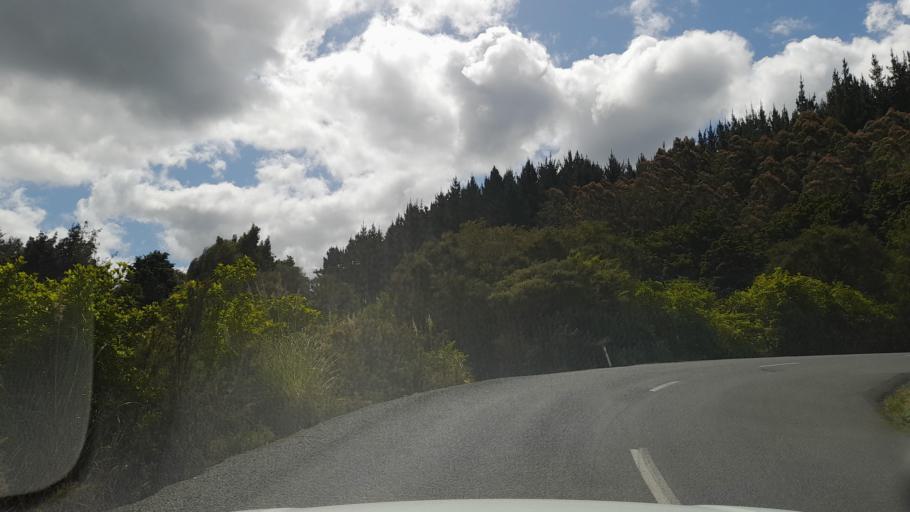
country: NZ
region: Northland
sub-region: Whangarei
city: Maungatapere
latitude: -35.6924
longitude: 174.0423
